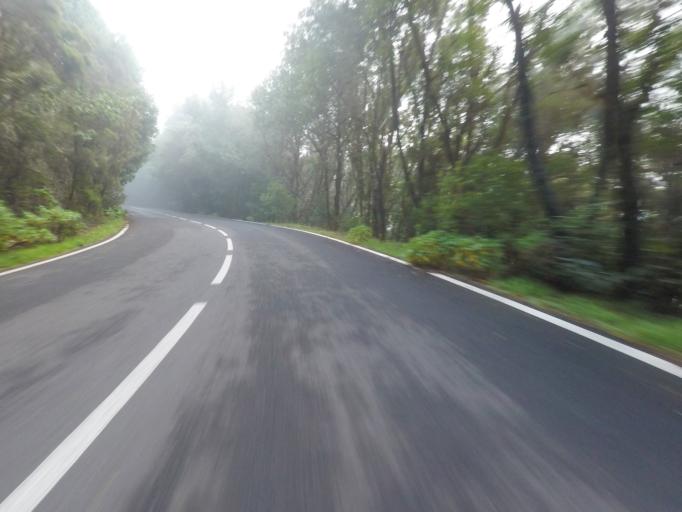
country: ES
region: Canary Islands
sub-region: Provincia de Santa Cruz de Tenerife
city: Alajero
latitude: 28.1150
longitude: -17.2188
